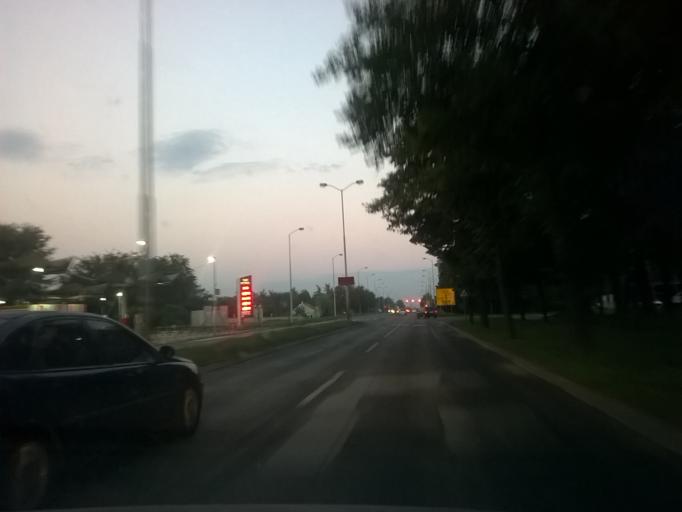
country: RS
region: Autonomna Pokrajina Vojvodina
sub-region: Juznobanatski Okrug
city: Pancevo
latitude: 44.8807
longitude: 20.6545
